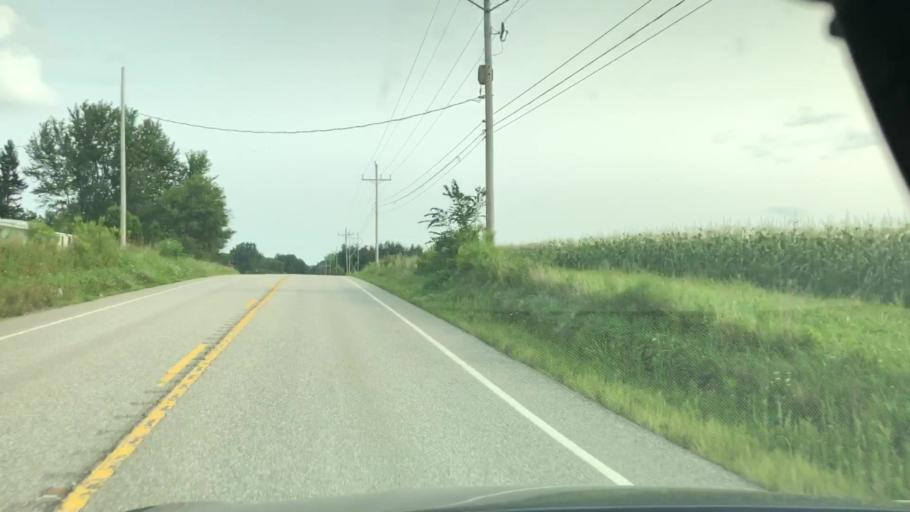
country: US
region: Pennsylvania
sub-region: Erie County
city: Union City
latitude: 41.9336
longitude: -79.8438
